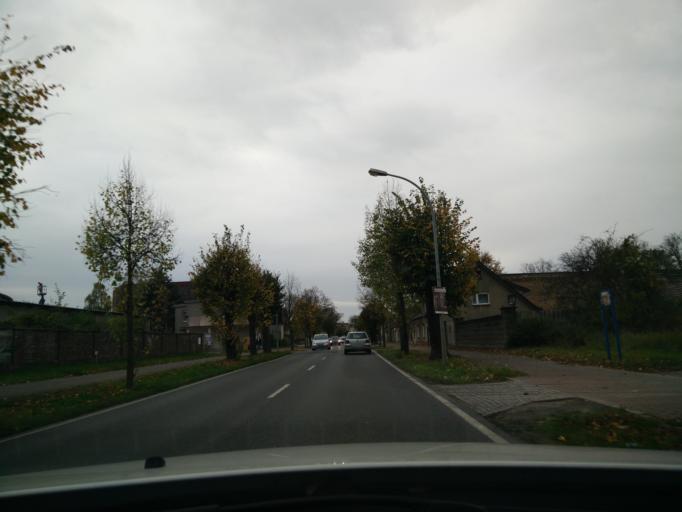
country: DE
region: Brandenburg
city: Velten
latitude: 52.6832
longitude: 13.1791
